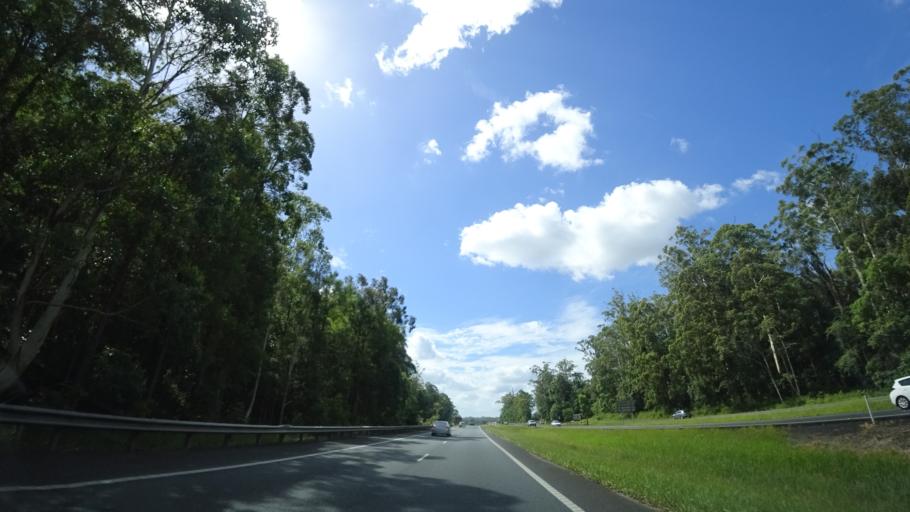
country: AU
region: Queensland
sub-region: Sunshine Coast
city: Buderim
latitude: -26.6982
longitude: 153.0124
